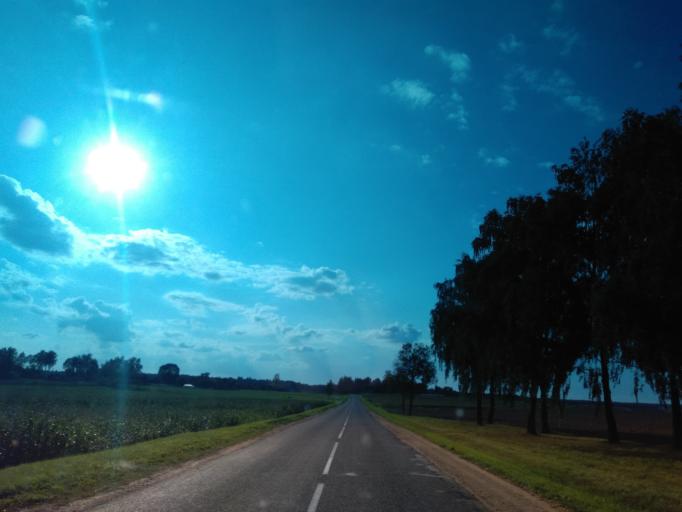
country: BY
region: Minsk
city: Kapyl'
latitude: 53.2045
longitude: 27.0365
